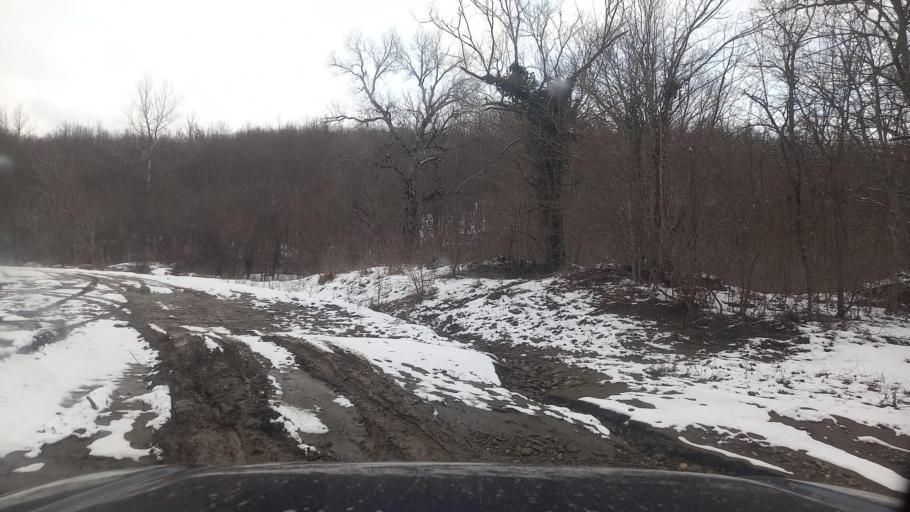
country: RU
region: Krasnodarskiy
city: Smolenskaya
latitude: 44.6575
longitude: 38.7689
